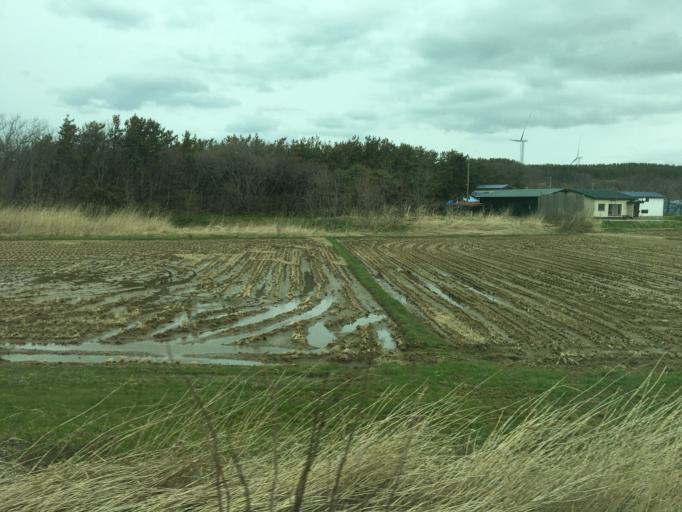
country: JP
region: Aomori
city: Shimokizukuri
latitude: 40.7870
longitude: 140.2415
